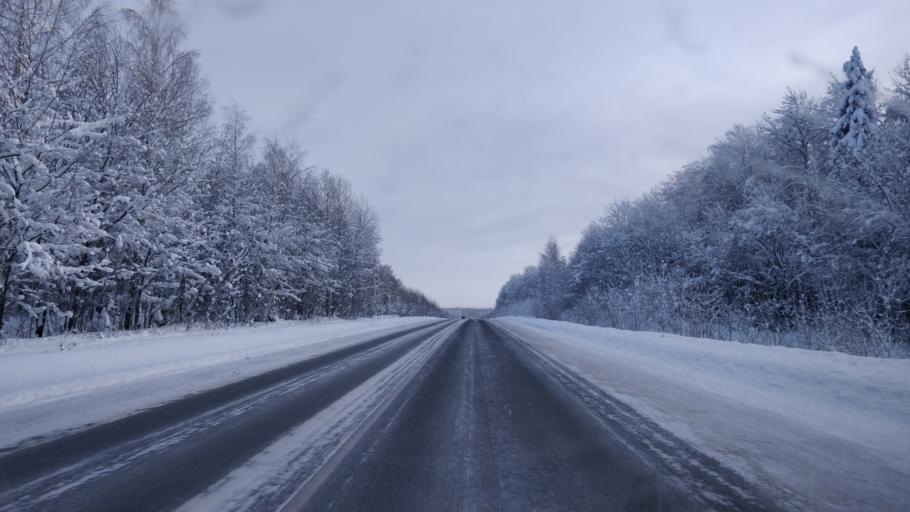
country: RU
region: Perm
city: Verkhnechusovskiye Gorodki
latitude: 58.2611
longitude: 56.9790
